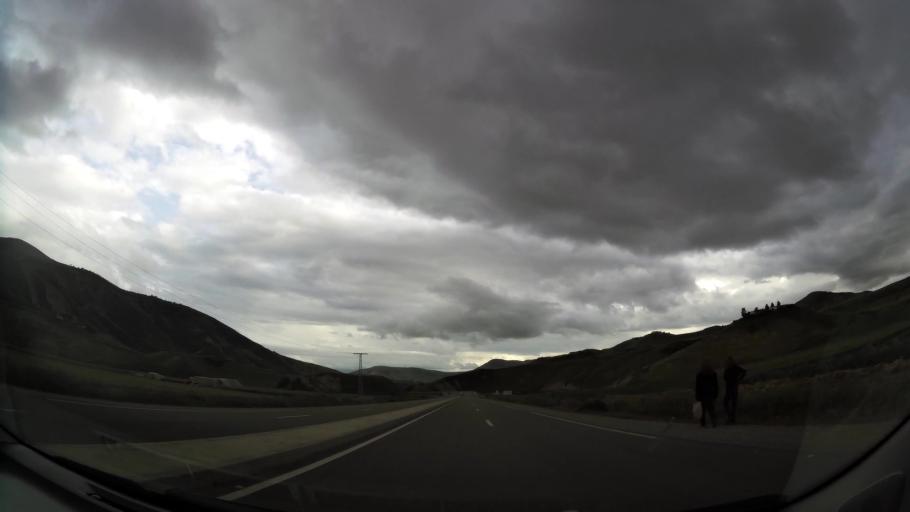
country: MA
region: Taza-Al Hoceima-Taounate
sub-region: Taza
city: Taza
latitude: 34.3283
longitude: -3.9494
